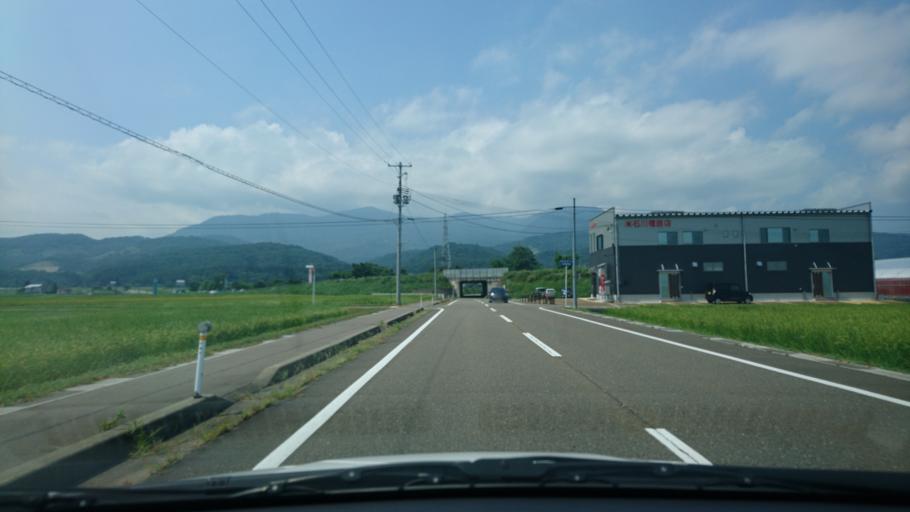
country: JP
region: Niigata
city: Arai
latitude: 37.0510
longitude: 138.2494
